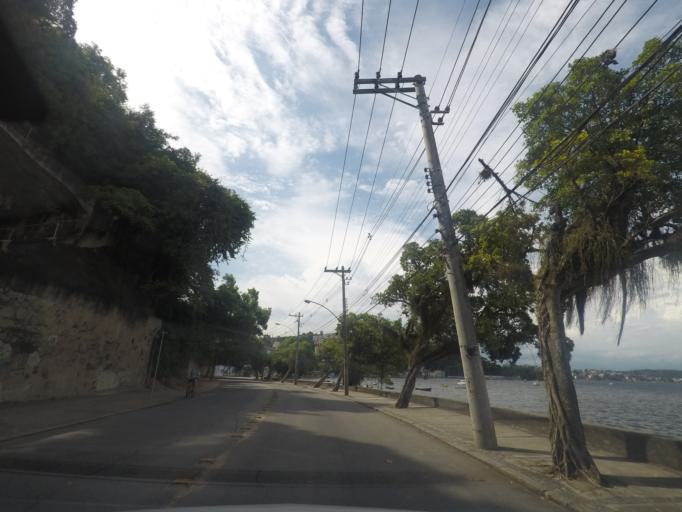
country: BR
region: Rio de Janeiro
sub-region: Rio De Janeiro
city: Rio de Janeiro
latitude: -22.8179
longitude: -43.1753
